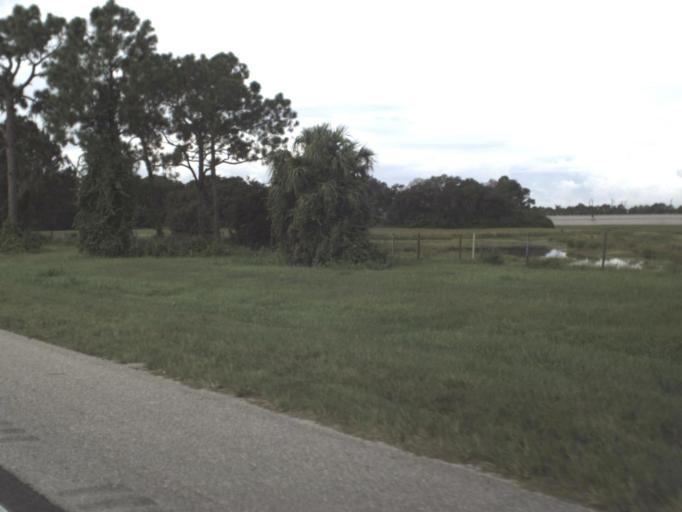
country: US
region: Florida
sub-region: Sarasota County
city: The Meadows
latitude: 27.3792
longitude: -82.4469
